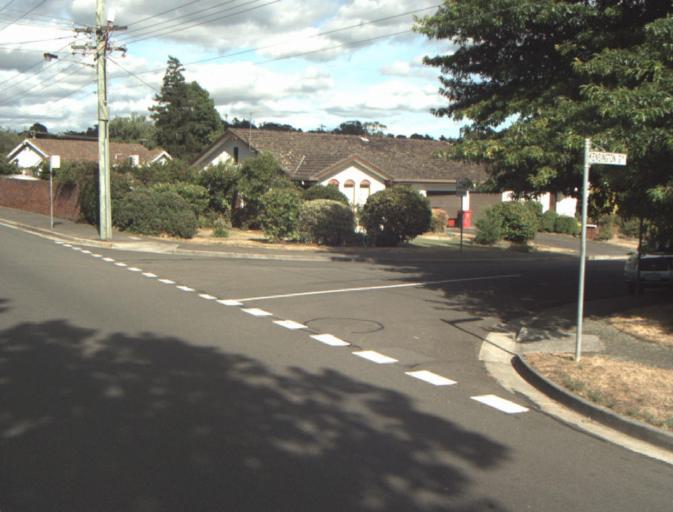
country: AU
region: Tasmania
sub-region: Launceston
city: Newstead
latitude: -41.4552
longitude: 147.1743
